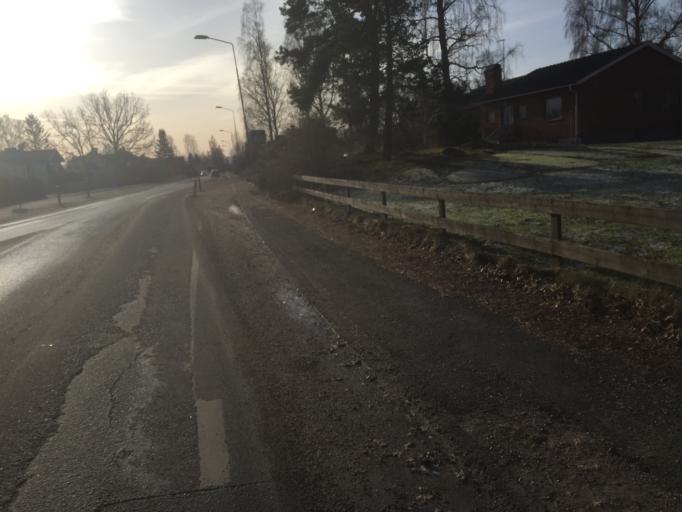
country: SE
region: Joenkoeping
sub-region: Aneby Kommun
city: Aneby
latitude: 57.8417
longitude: 14.8042
